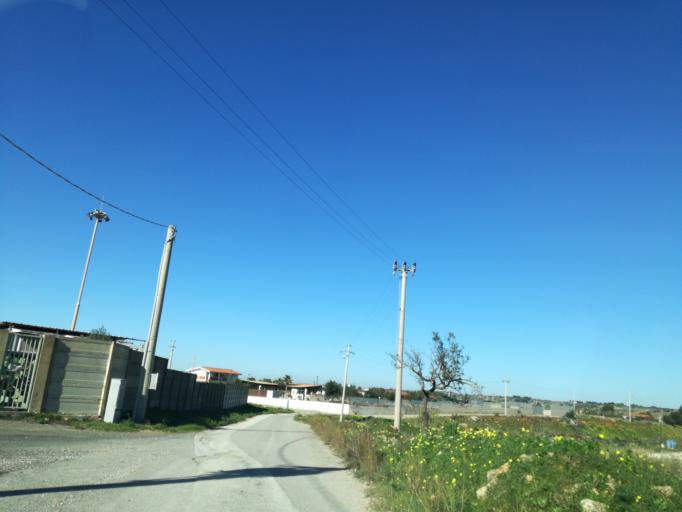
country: IT
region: Sicily
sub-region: Provincia di Caltanissetta
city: Niscemi
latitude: 37.0587
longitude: 14.3581
